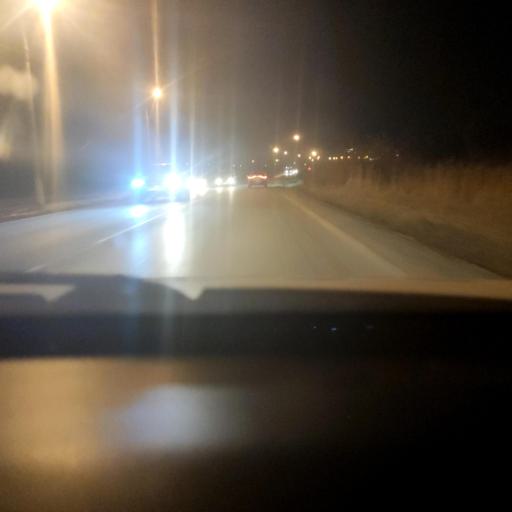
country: RU
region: Perm
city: Perm
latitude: 58.0968
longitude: 56.3975
